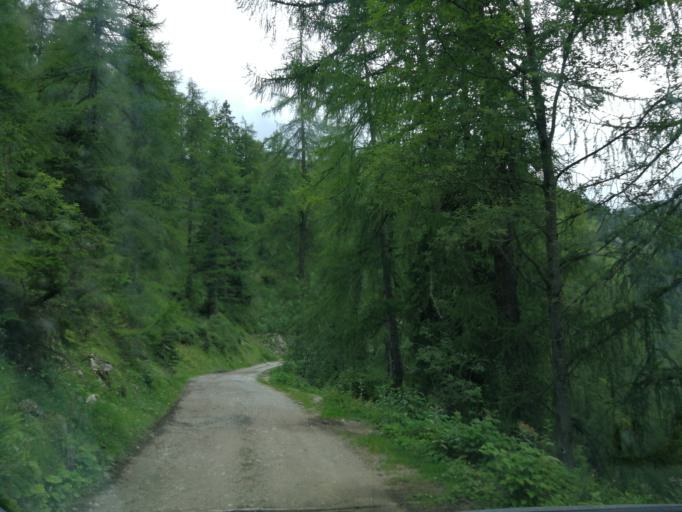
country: IT
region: Trentino-Alto Adige
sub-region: Provincia di Trento
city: Brione
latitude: 45.9379
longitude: 10.5415
